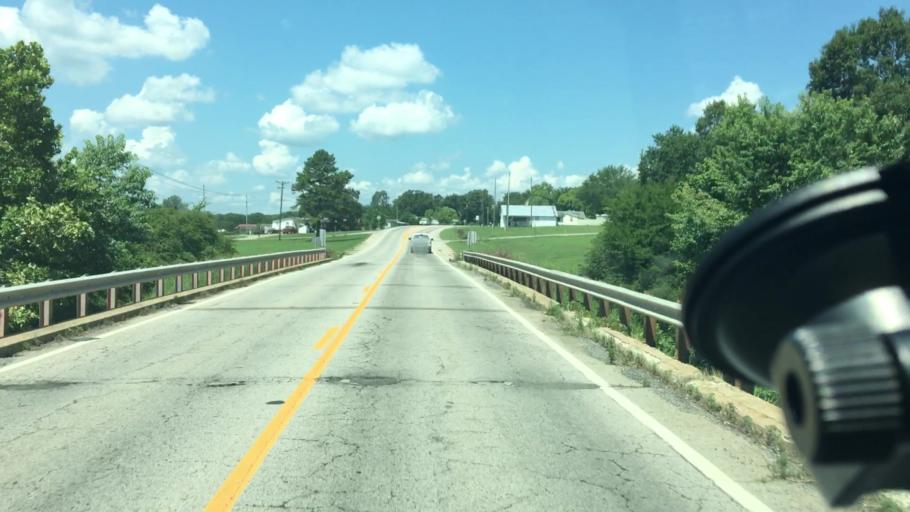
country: US
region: Arkansas
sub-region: Sebastian County
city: Lavaca
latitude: 35.2929
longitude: -94.1327
